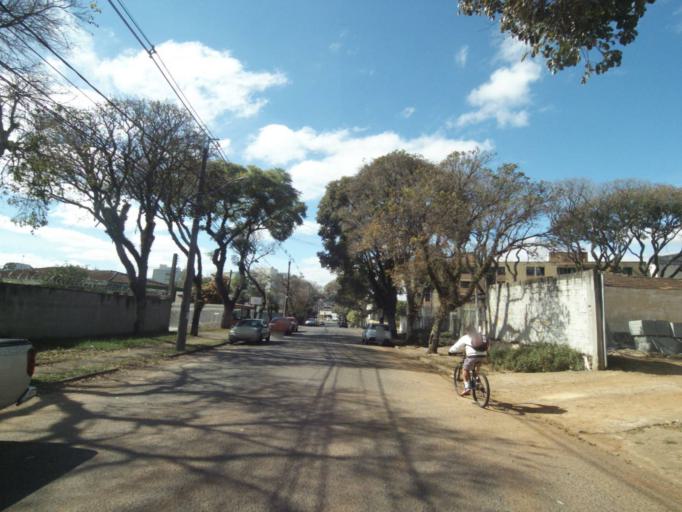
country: BR
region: Parana
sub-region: Curitiba
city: Curitiba
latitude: -25.4627
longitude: -49.2801
